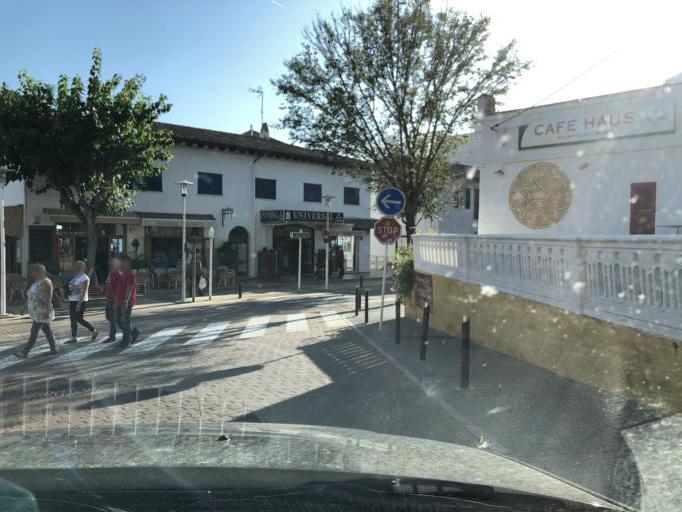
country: ES
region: Balearic Islands
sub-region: Illes Balears
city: Camp de Mar
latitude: 39.5381
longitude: 2.4498
